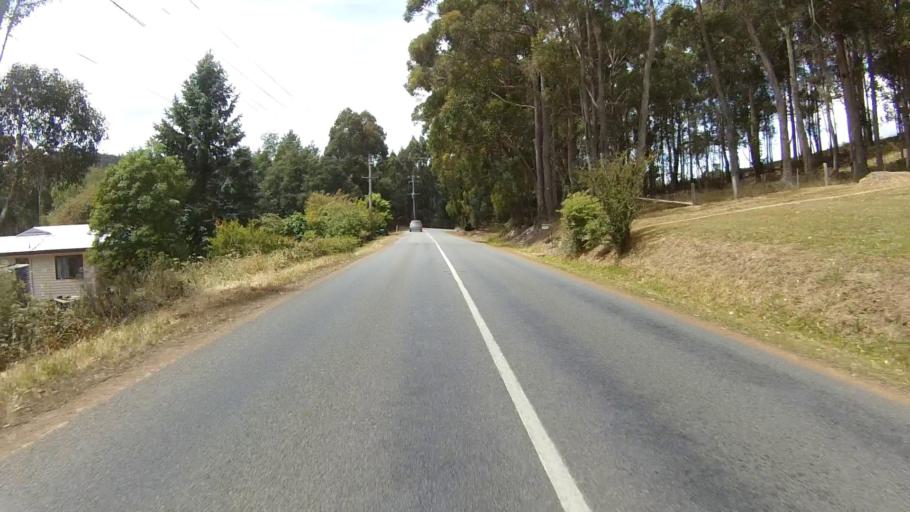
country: AU
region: Tasmania
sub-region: Kingborough
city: Kettering
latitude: -43.1054
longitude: 147.2386
